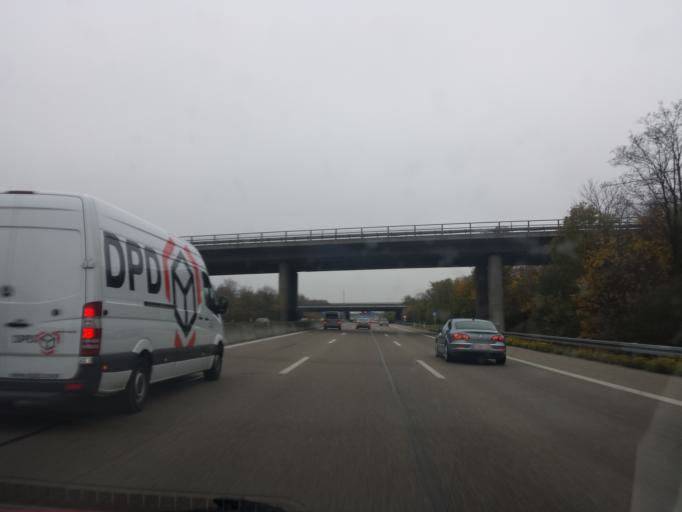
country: DE
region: Bavaria
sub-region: Upper Bavaria
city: Garching bei Munchen
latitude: 48.2234
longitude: 11.6303
